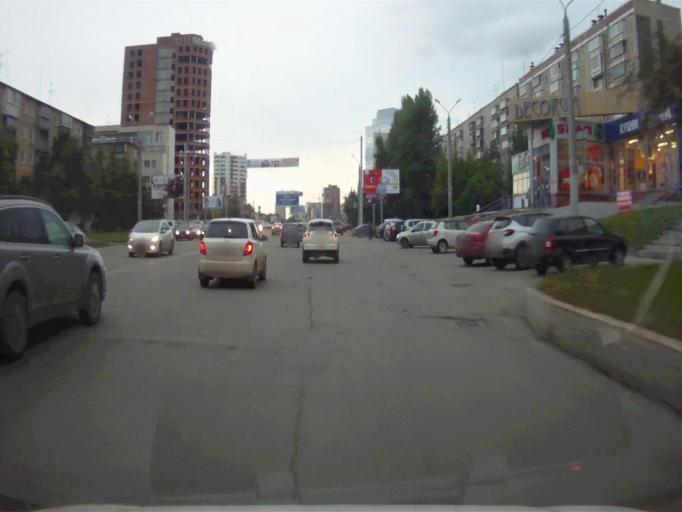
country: RU
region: Chelyabinsk
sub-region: Gorod Chelyabinsk
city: Chelyabinsk
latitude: 55.1527
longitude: 61.3825
